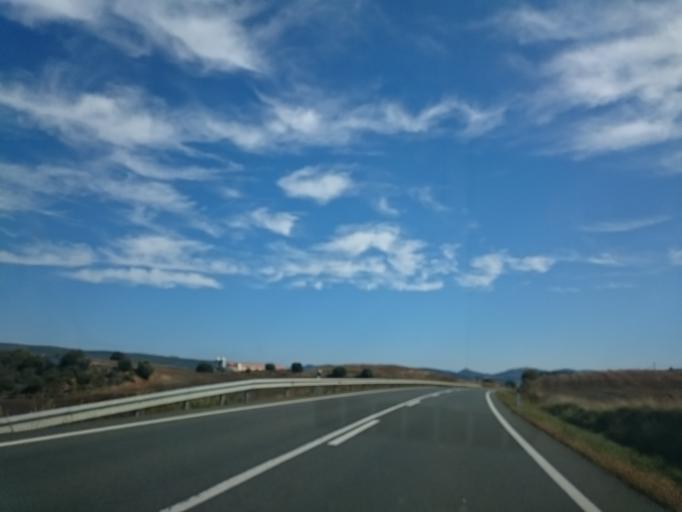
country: ES
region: Aragon
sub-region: Provincia de Huesca
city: Benavarri / Benabarre
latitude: 42.1124
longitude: 0.5202
